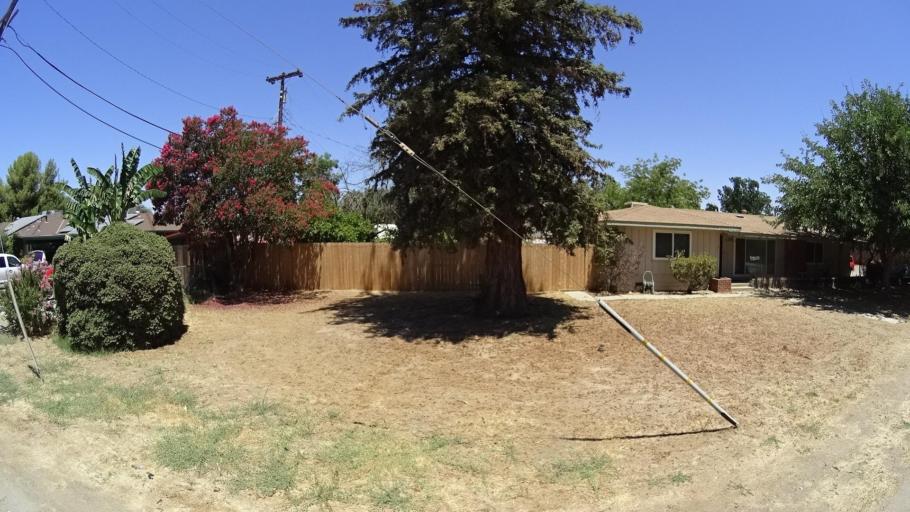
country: US
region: California
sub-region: Fresno County
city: Tarpey Village
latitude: 36.7822
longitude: -119.7436
